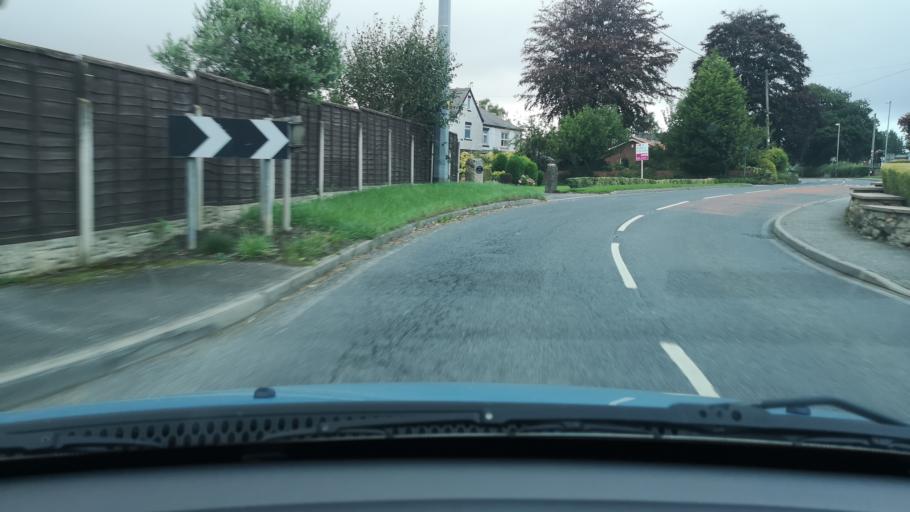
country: GB
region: England
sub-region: City and Borough of Wakefield
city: Badsworth
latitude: 53.6399
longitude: -1.2823
